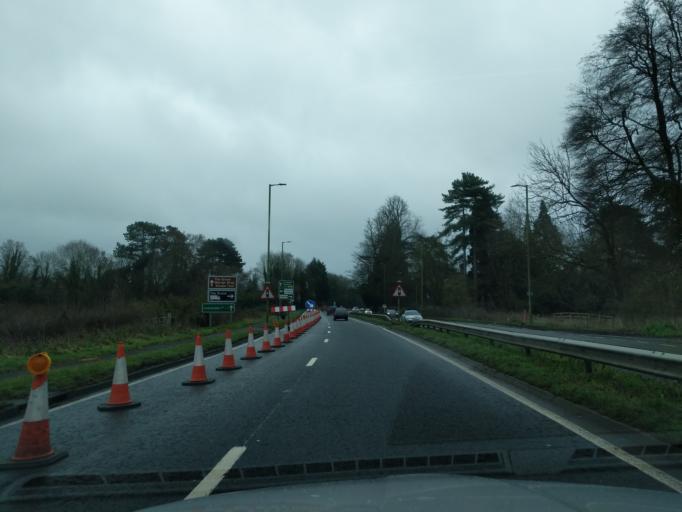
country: GB
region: England
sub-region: Hertfordshire
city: Kings Langley
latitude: 51.6951
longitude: -0.4390
